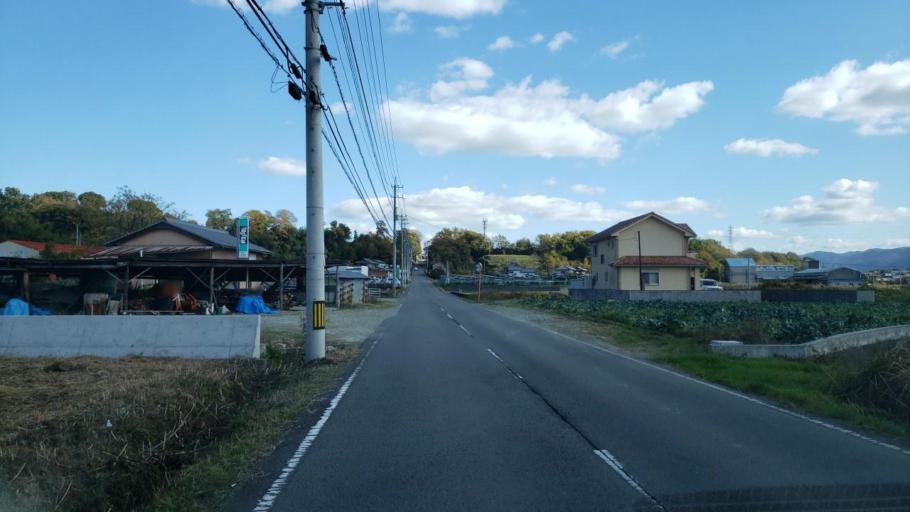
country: JP
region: Tokushima
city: Wakimachi
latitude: 34.0812
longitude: 134.2092
